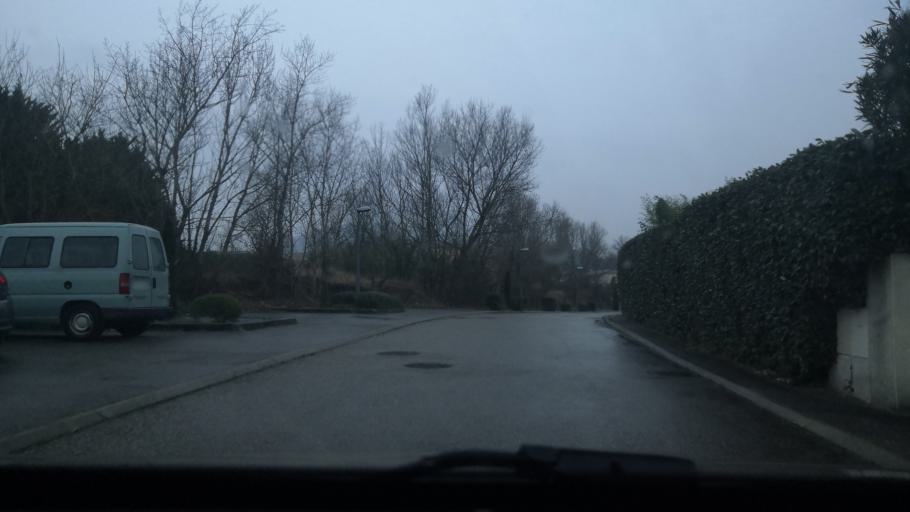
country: FR
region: Rhone-Alpes
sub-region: Departement de la Drome
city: Montboucher-sur-Jabron
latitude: 44.5413
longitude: 4.7988
